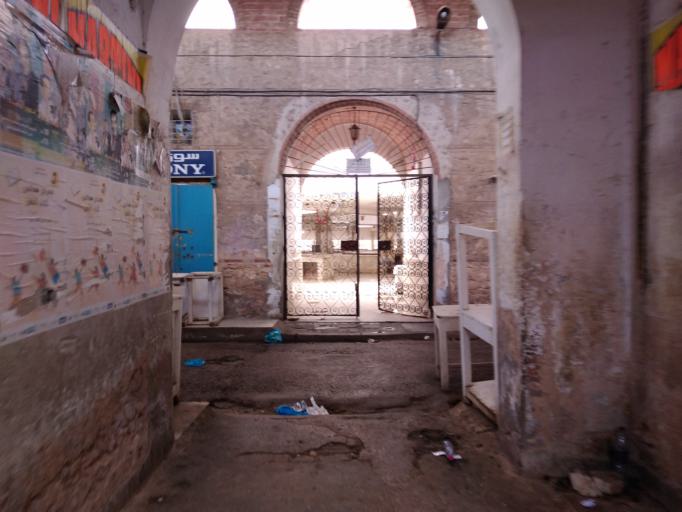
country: TN
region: Safaqis
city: Sfax
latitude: 34.7379
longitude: 10.7594
